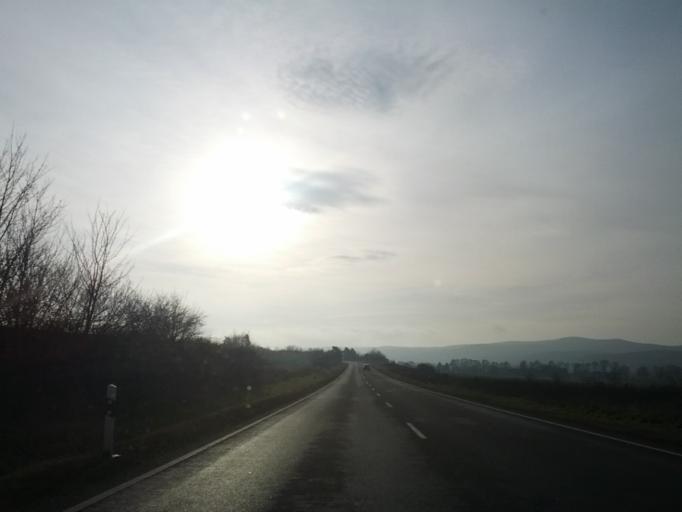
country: DE
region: Thuringia
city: Breitungen
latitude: 50.7829
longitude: 10.3162
